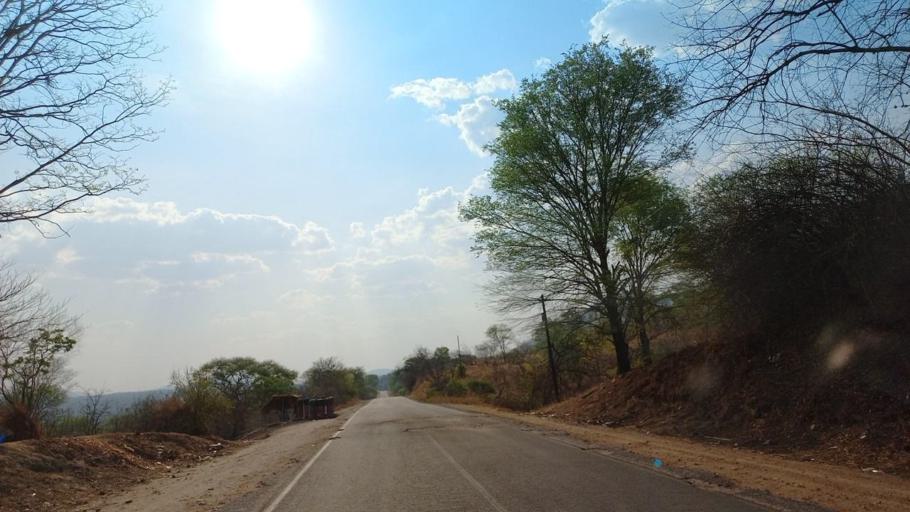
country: ZM
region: Lusaka
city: Luangwa
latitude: -14.9825
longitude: 30.1735
